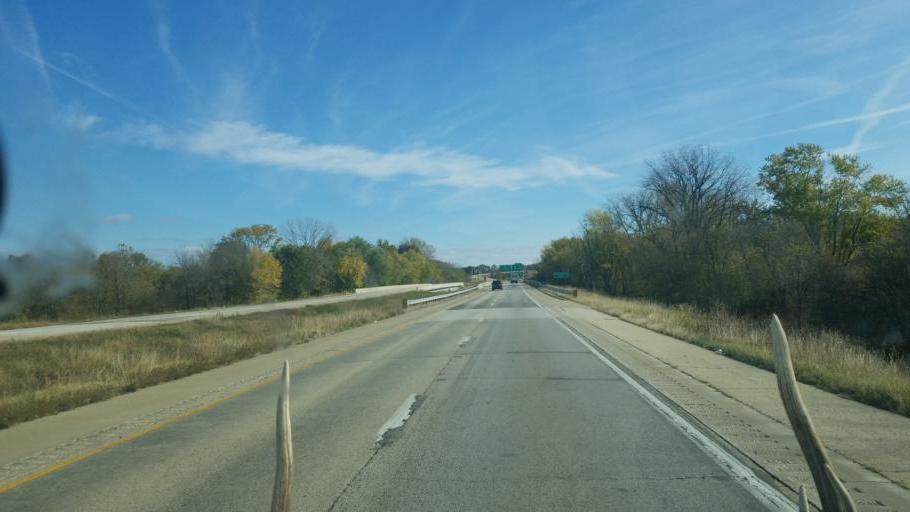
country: US
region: Illinois
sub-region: Effingham County
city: Effingham
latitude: 39.0896
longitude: -88.5972
